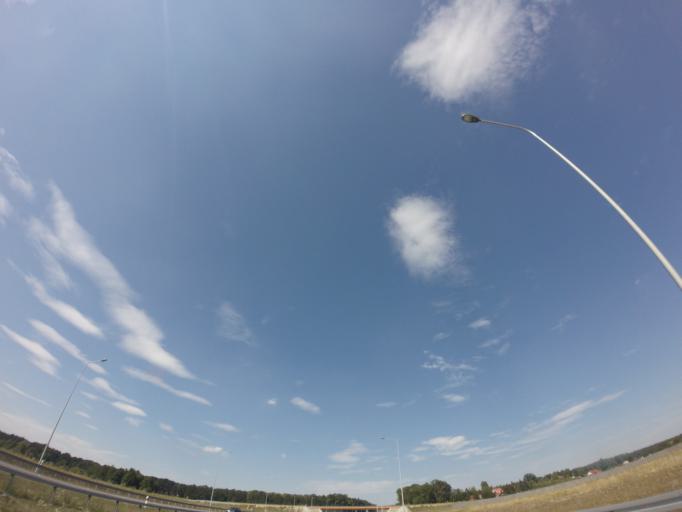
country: PL
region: Lower Silesian Voivodeship
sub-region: Legnica
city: Legnica
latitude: 51.2843
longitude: 16.1509
